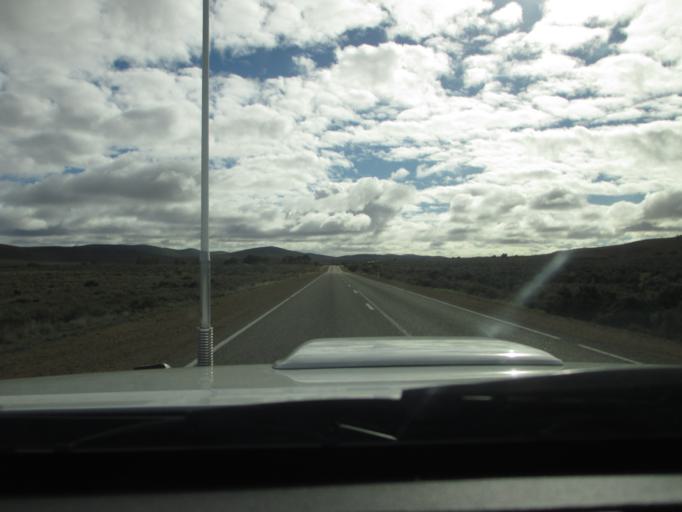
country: AU
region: South Australia
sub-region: Flinders Ranges
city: Quorn
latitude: -32.2367
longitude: 138.5134
